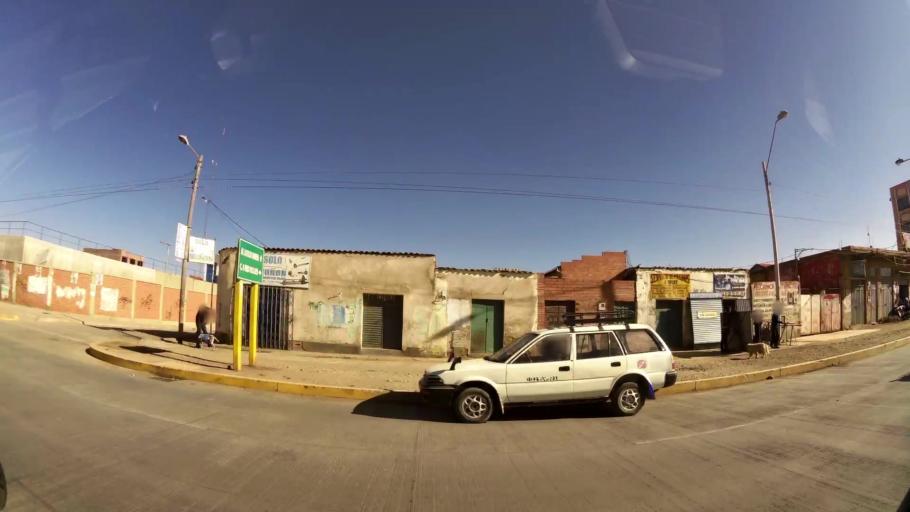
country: BO
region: La Paz
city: La Paz
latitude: -16.5311
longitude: -68.1877
